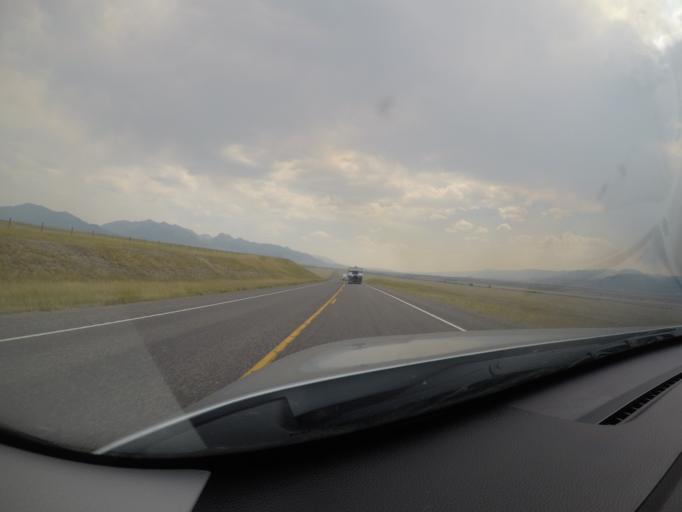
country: US
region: Montana
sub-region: Madison County
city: Virginia City
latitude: 45.1439
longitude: -111.6772
